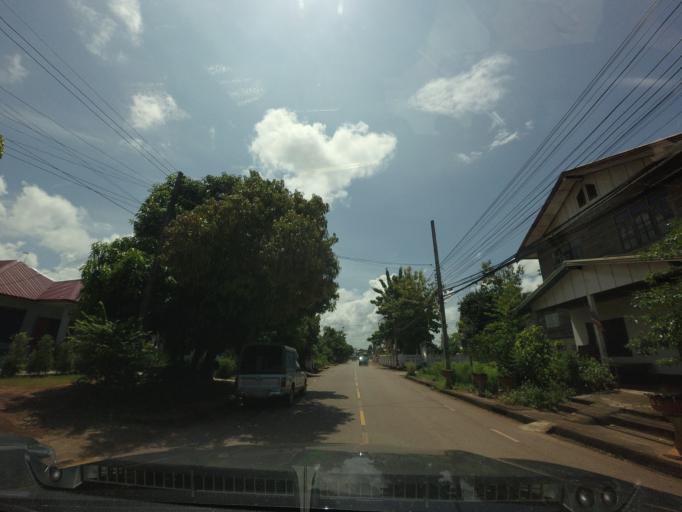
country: TH
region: Changwat Udon Thani
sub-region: Amphoe Ban Phue
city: Ban Phue
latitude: 17.6938
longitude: 102.4662
